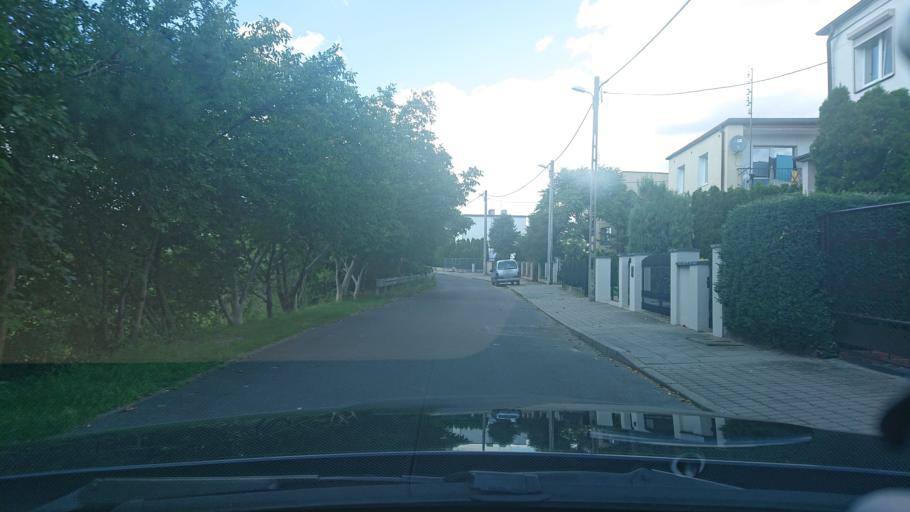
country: PL
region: Greater Poland Voivodeship
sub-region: Powiat gnieznienski
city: Gniezno
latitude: 52.5349
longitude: 17.6339
